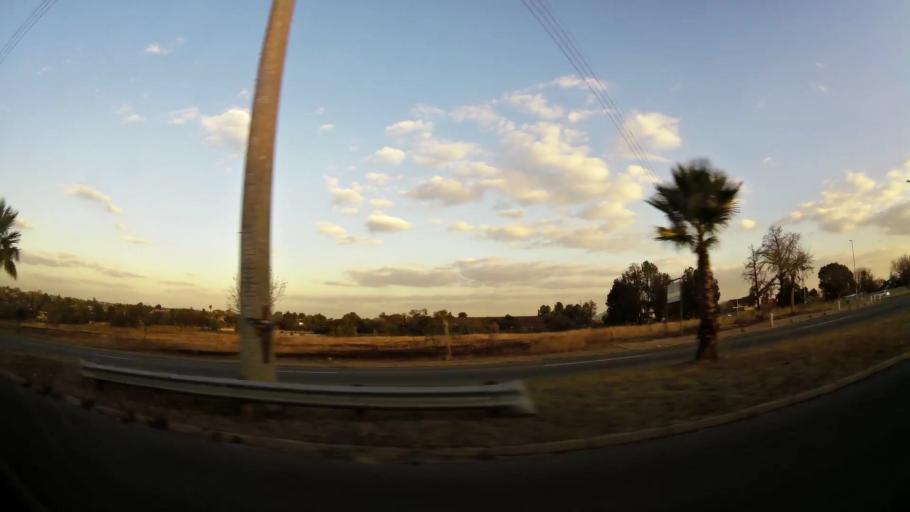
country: ZA
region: Gauteng
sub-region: West Rand District Municipality
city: Krugersdorp
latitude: -26.0801
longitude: 27.7668
